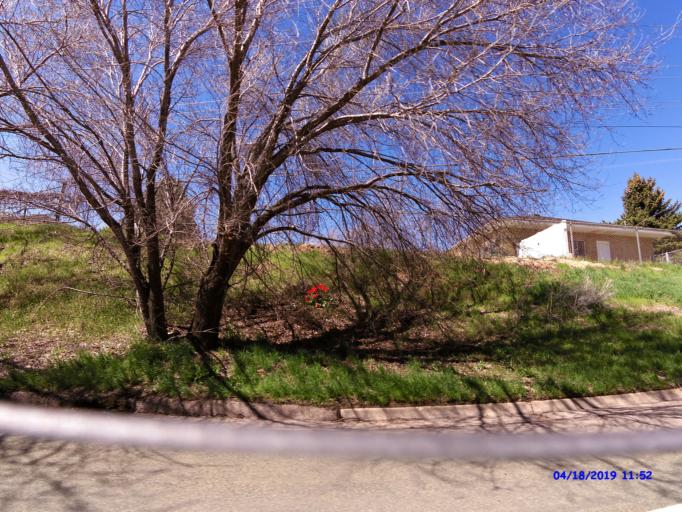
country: US
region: Utah
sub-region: Weber County
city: Ogden
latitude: 41.2463
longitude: -111.9480
